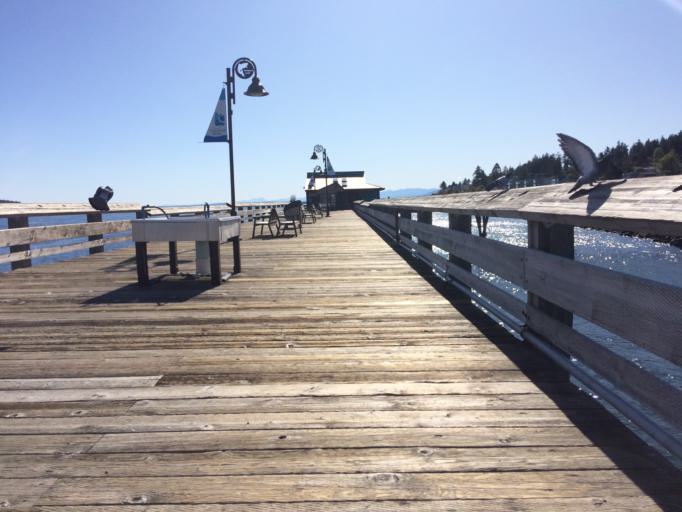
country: CA
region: British Columbia
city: Campbell River
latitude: 50.0216
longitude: -125.2358
